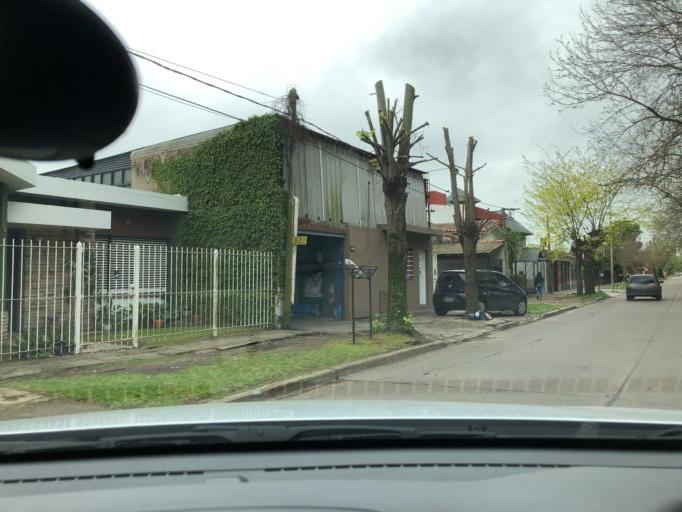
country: AR
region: Buenos Aires
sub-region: Partido de La Plata
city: La Plata
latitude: -34.8732
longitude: -58.0463
